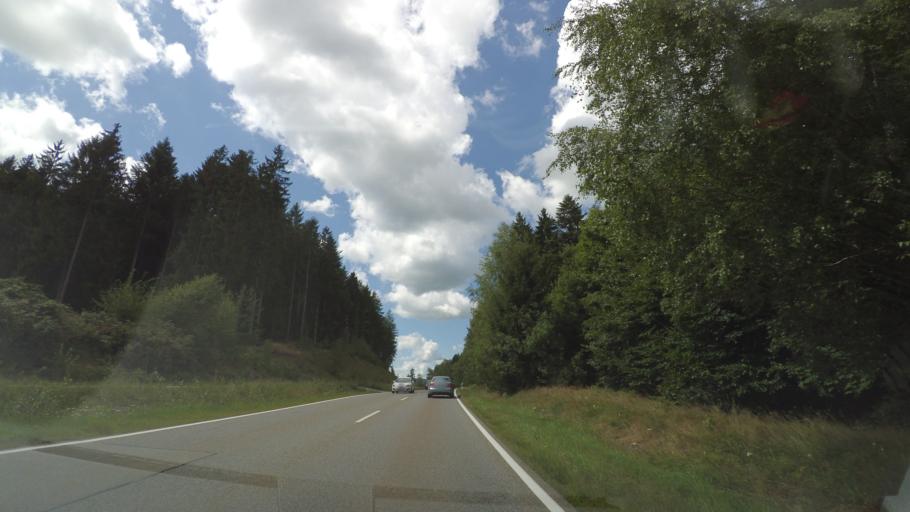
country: DE
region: Bavaria
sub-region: Lower Bavaria
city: Teisnach
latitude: 49.0466
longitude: 13.0142
